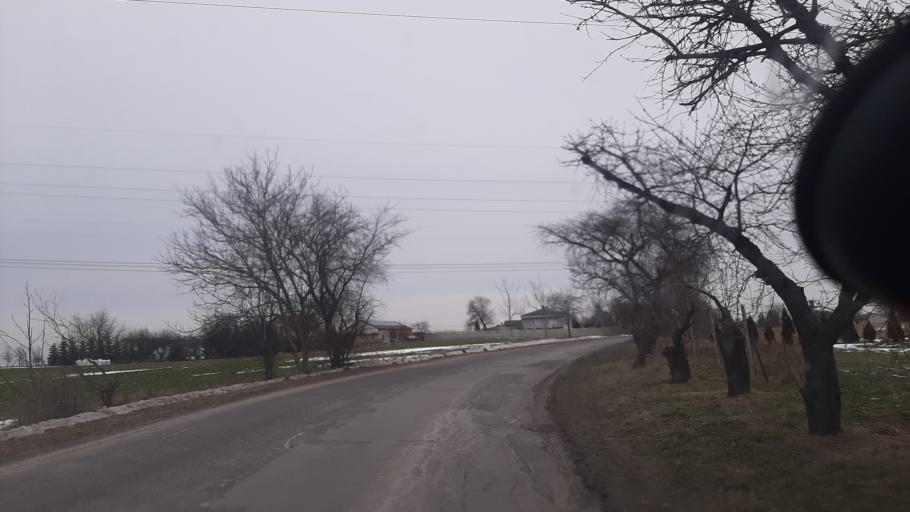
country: PL
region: Lublin Voivodeship
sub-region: Powiat lubelski
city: Jakubowice Murowane
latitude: 51.2946
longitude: 22.6278
